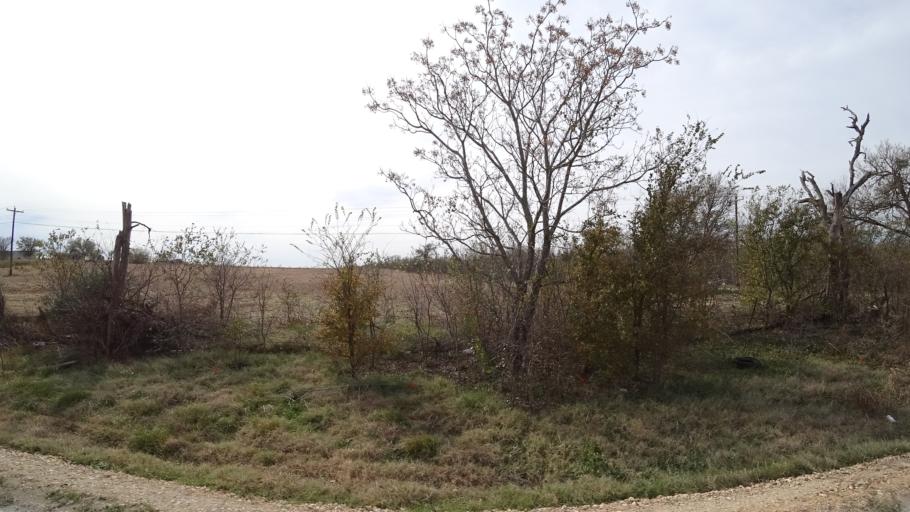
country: US
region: Texas
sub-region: Travis County
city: Garfield
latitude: 30.1303
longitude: -97.6053
